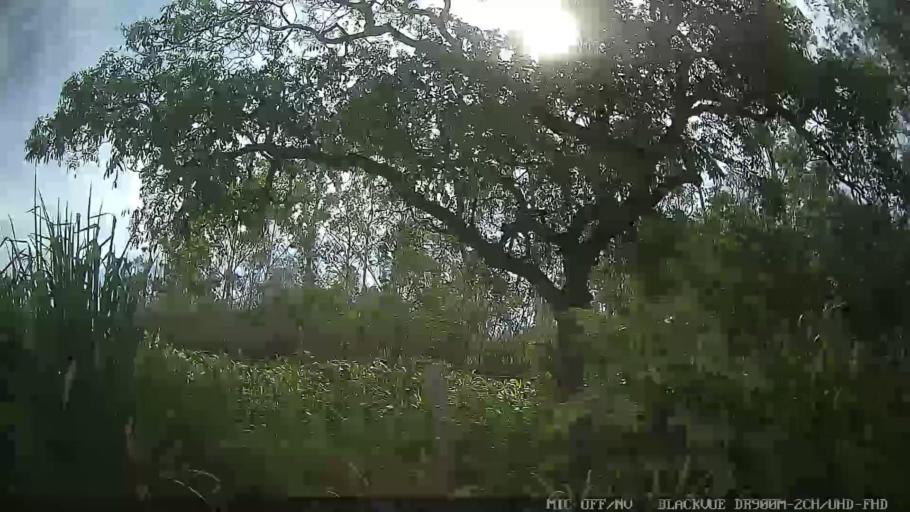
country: BR
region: Sao Paulo
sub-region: Conchas
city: Conchas
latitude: -23.0464
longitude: -47.9930
